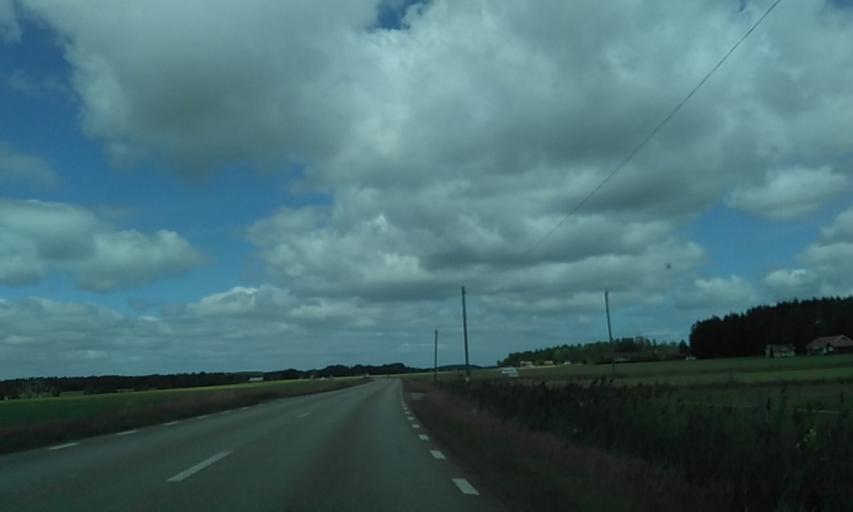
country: SE
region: Vaestra Goetaland
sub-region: Grastorps Kommun
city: Graestorp
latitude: 58.2792
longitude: 12.6752
